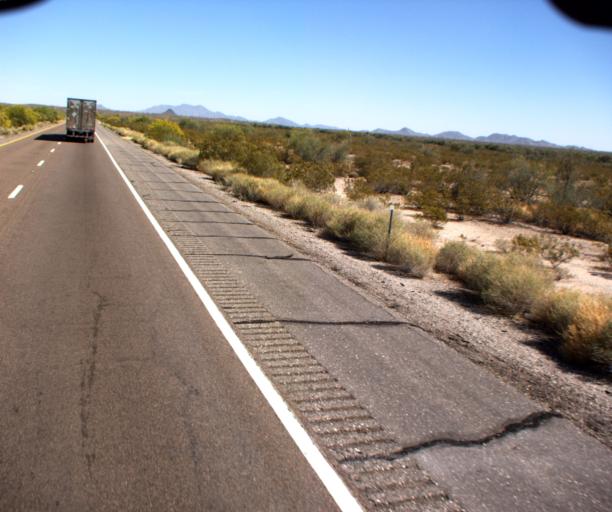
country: US
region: Arizona
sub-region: Maricopa County
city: Gila Bend
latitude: 32.8528
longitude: -112.3663
